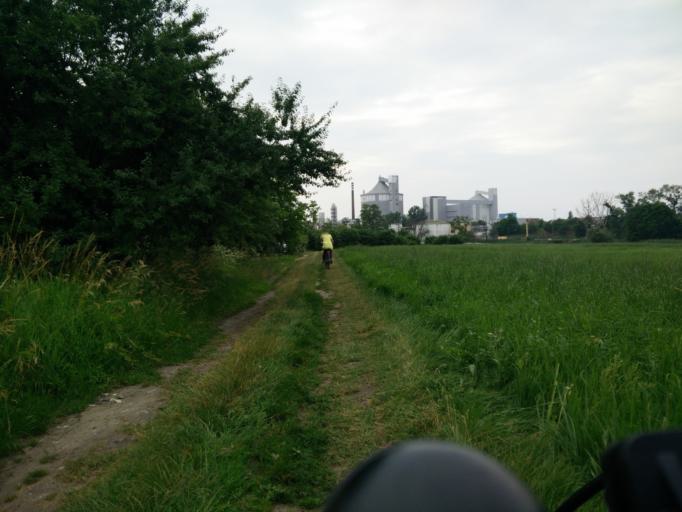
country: PL
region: Greater Poland Voivodeship
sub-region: Powiat sredzki
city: Sroda Wielkopolska
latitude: 52.2146
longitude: 17.2842
